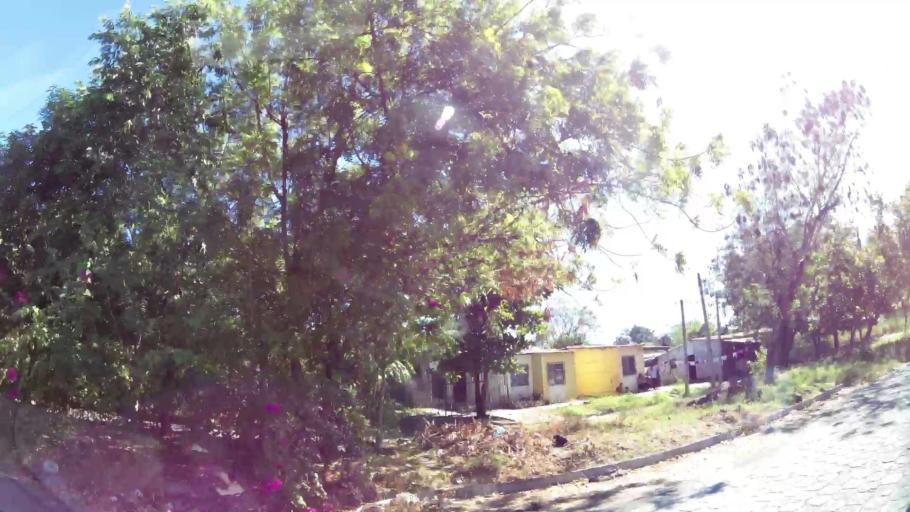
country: SV
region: San Miguel
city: San Miguel
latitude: 13.4954
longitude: -88.1647
